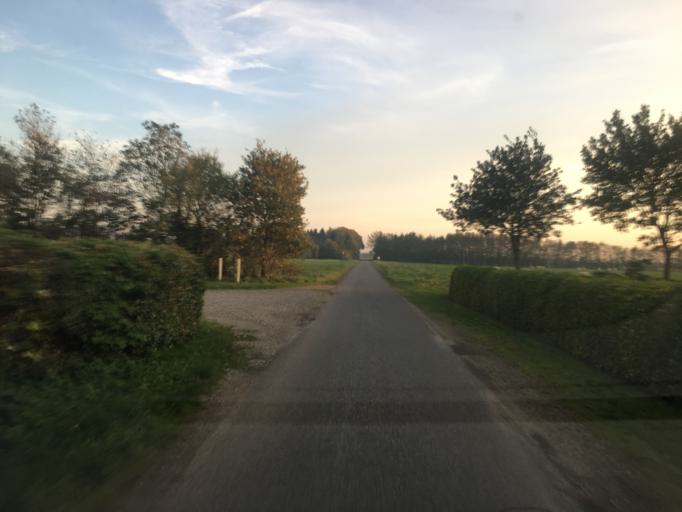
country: DK
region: South Denmark
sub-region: Aabenraa Kommune
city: Tinglev
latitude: 55.0280
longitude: 9.1266
